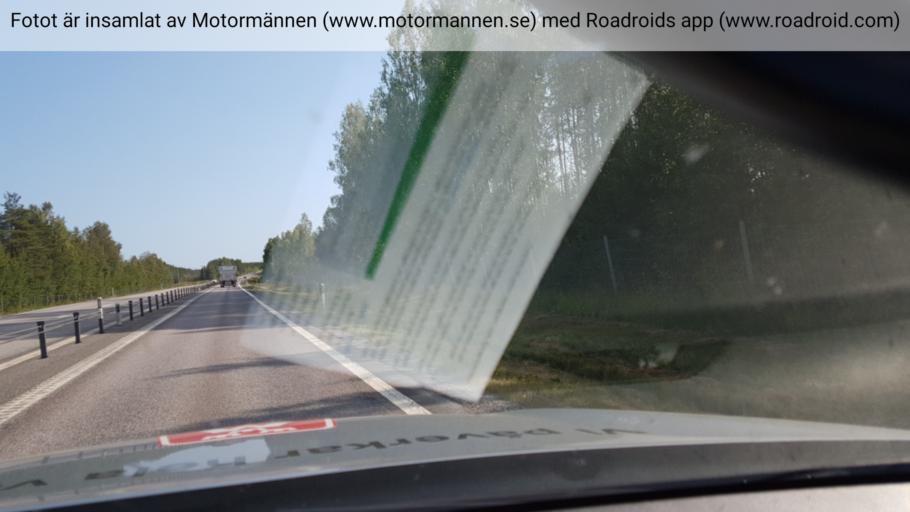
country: SE
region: Norrbotten
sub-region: Pitea Kommun
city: Hortlax
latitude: 65.2887
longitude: 21.4348
